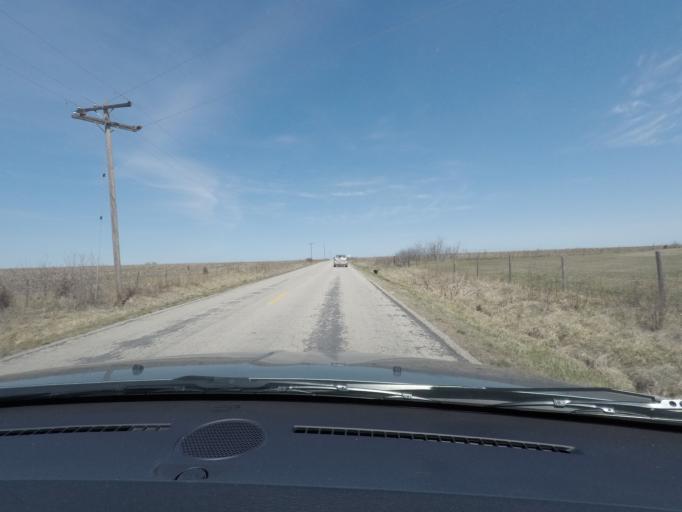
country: US
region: Kansas
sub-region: Lyon County
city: Emporia
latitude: 38.6291
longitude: -96.1696
